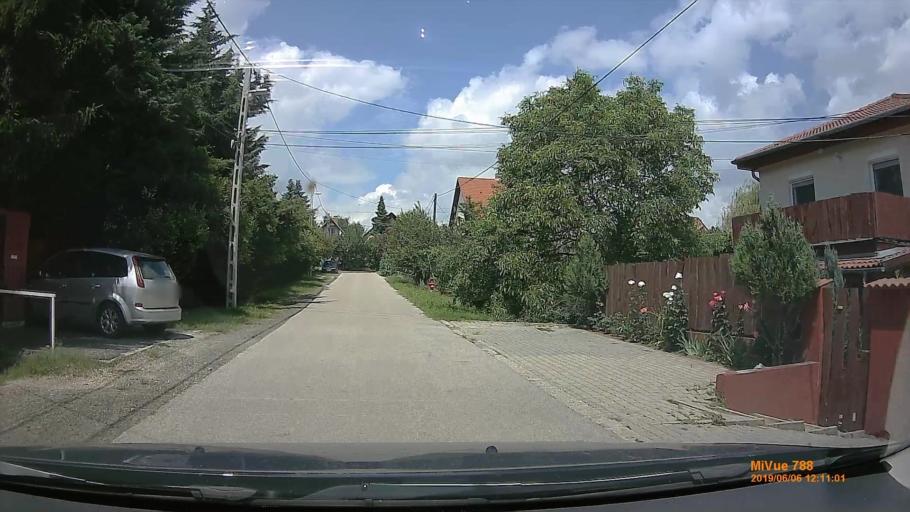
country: HU
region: Pest
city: Kerepes
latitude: 47.5717
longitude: 19.2621
